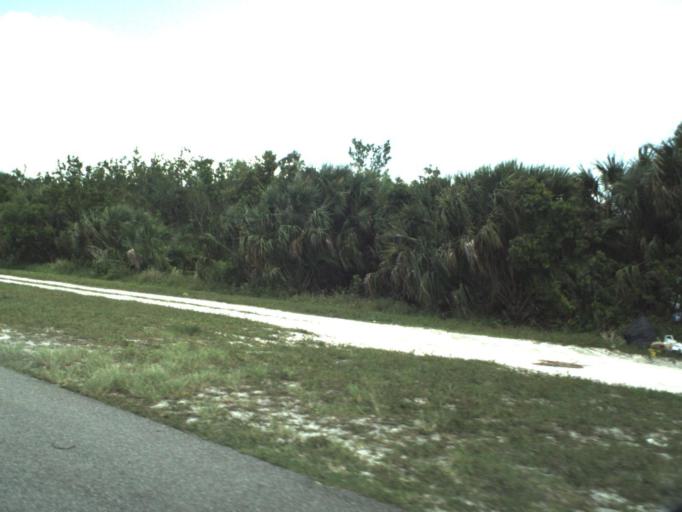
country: US
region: Florida
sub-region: Brevard County
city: Cocoa
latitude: 28.4046
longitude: -80.7213
